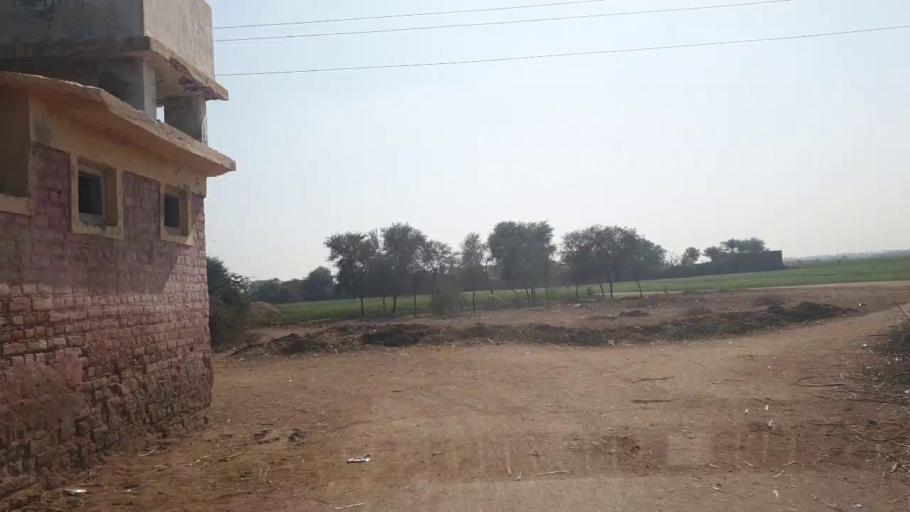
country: PK
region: Sindh
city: Shahdadpur
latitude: 26.0460
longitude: 68.4563
